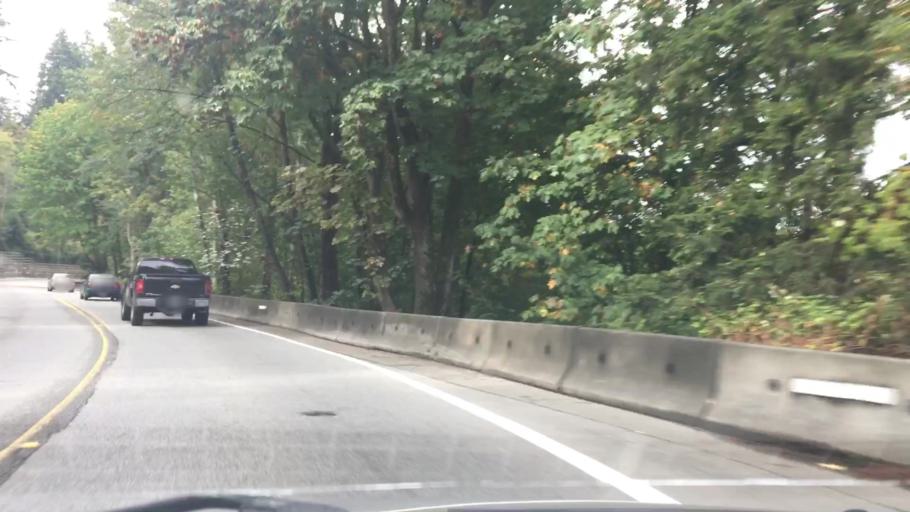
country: CA
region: British Columbia
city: Langley
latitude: 49.1054
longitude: -122.5675
